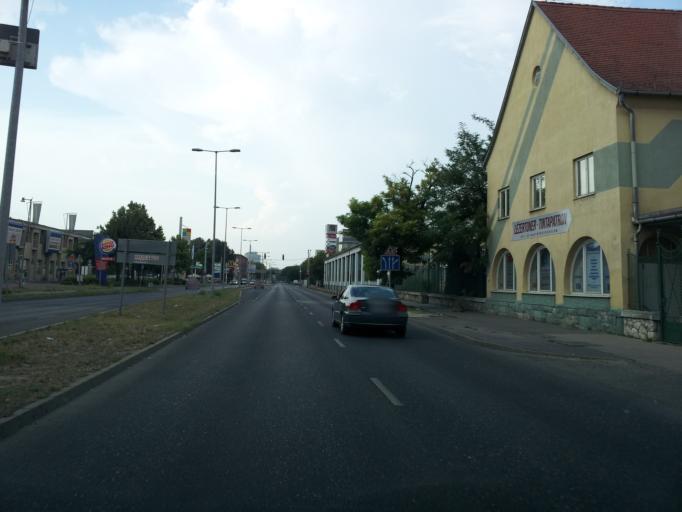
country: HU
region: Budapest
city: Budapest XI. keruelet
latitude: 47.4598
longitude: 19.0524
